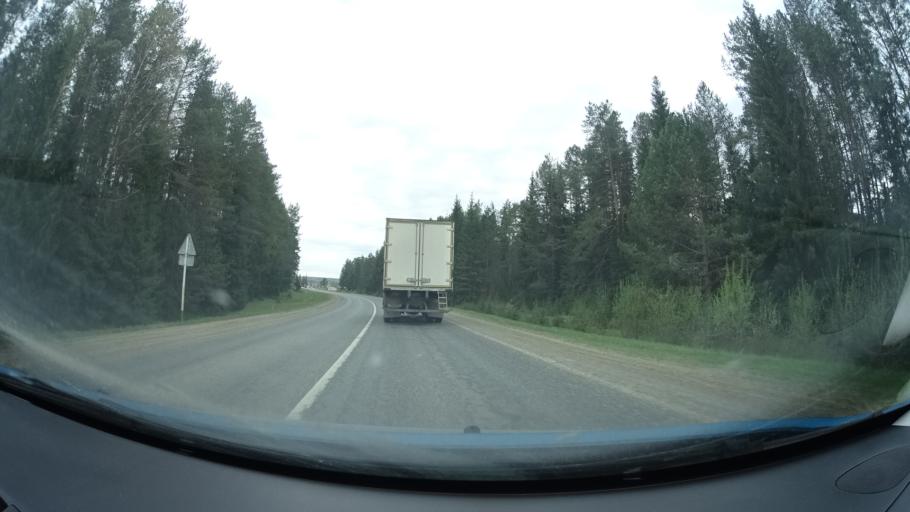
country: RU
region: Perm
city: Yugo-Kamskiy
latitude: 57.5614
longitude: 55.6794
